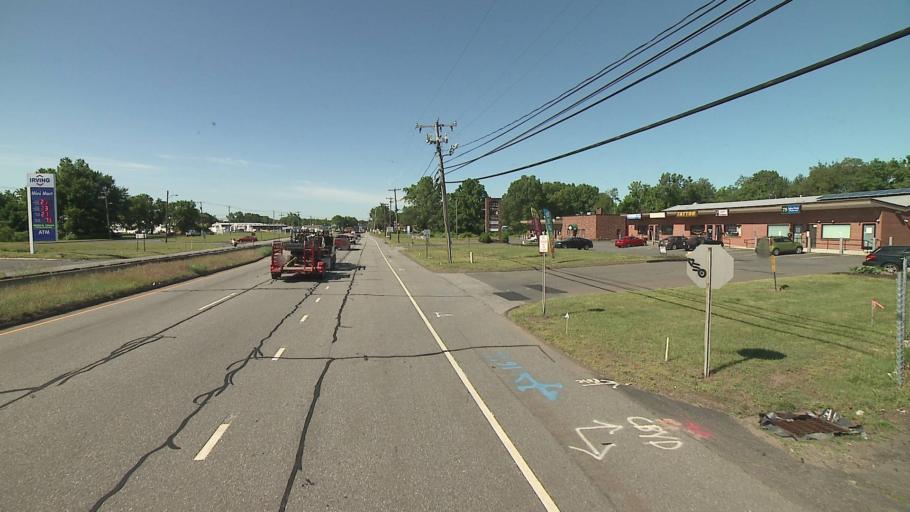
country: US
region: Connecticut
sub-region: Hartford County
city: East Hartford
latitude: 41.8015
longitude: -72.6173
